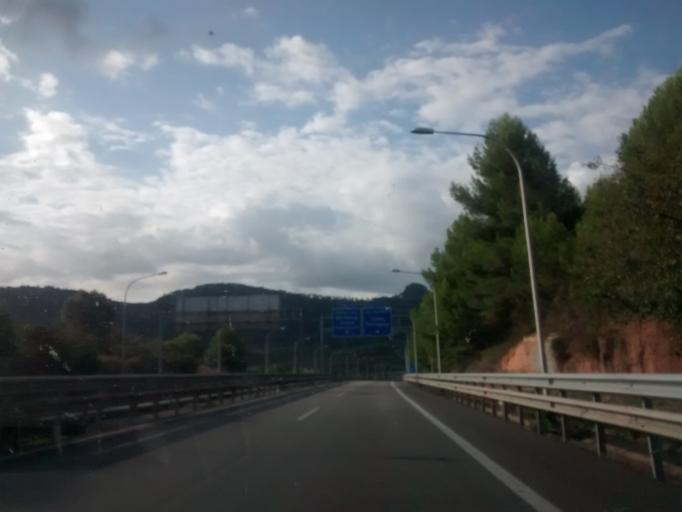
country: ES
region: Catalonia
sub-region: Provincia de Barcelona
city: Martorell
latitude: 41.4730
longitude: 1.9101
